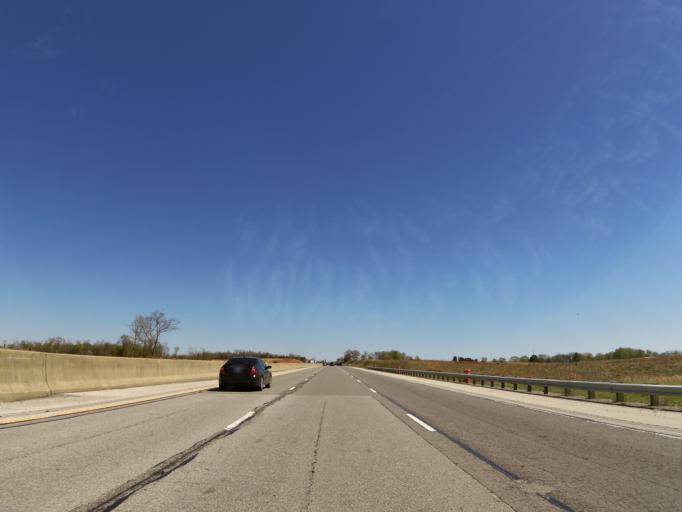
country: US
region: Kentucky
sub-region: Warren County
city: Bowling Green
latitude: 37.0114
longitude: -86.3344
